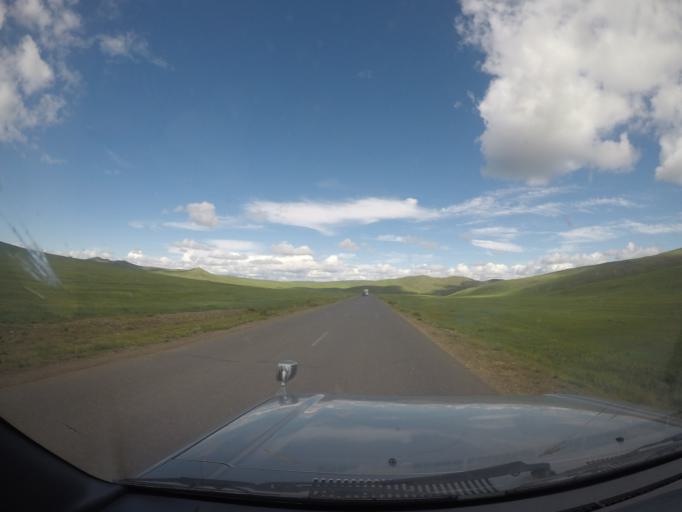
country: MN
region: Hentiy
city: Bayanbulag
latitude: 47.4555
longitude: 109.8108
